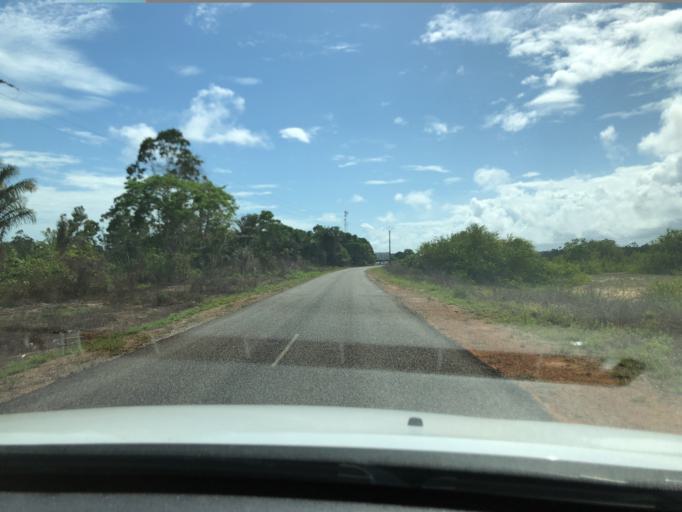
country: GF
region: Guyane
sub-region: Guyane
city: Mana
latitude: 5.6726
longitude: -53.7899
